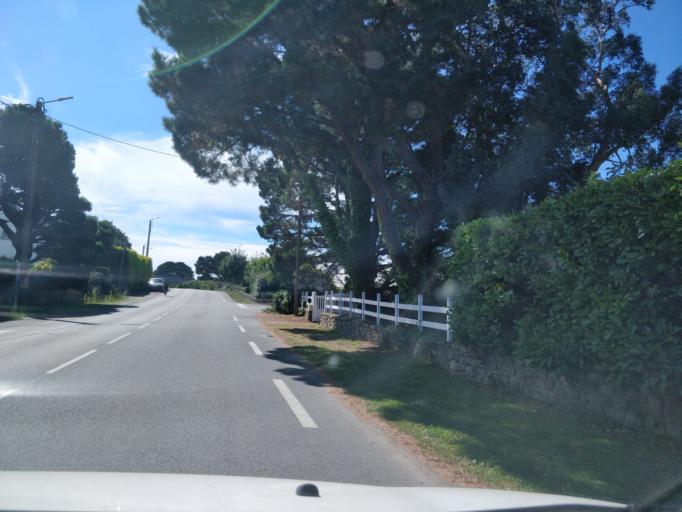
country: FR
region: Brittany
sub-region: Departement du Morbihan
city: Saint-Philibert
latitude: 47.5753
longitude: -3.0004
